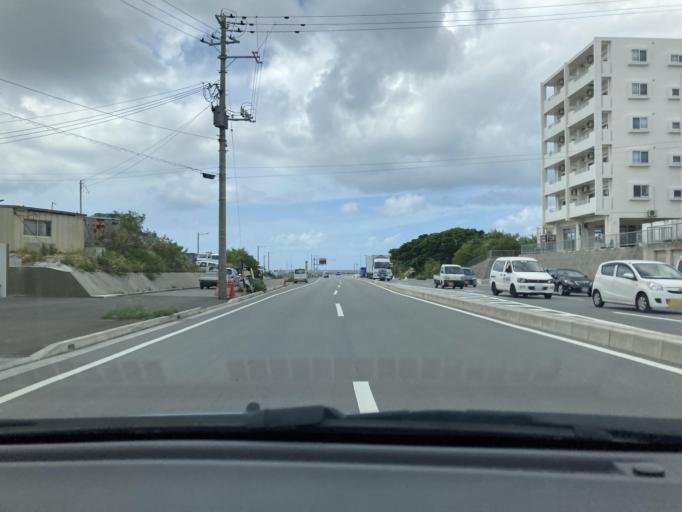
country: JP
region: Okinawa
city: Ginowan
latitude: 26.2696
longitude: 127.7089
